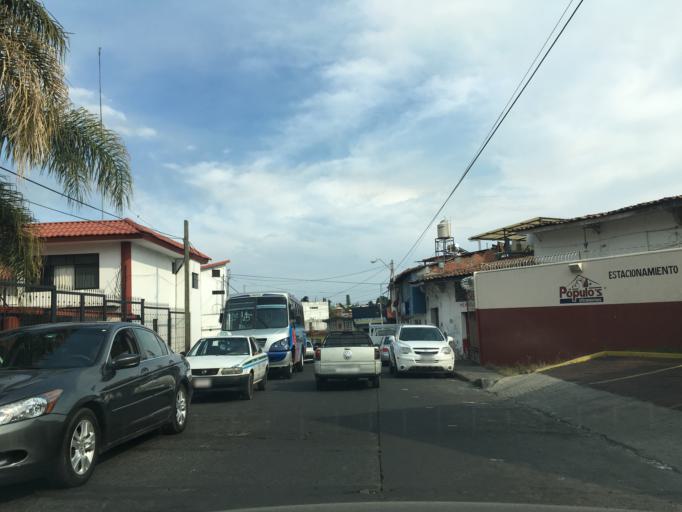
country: MX
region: Michoacan
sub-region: Uruapan
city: Uruapan
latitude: 19.4176
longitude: -102.0602
